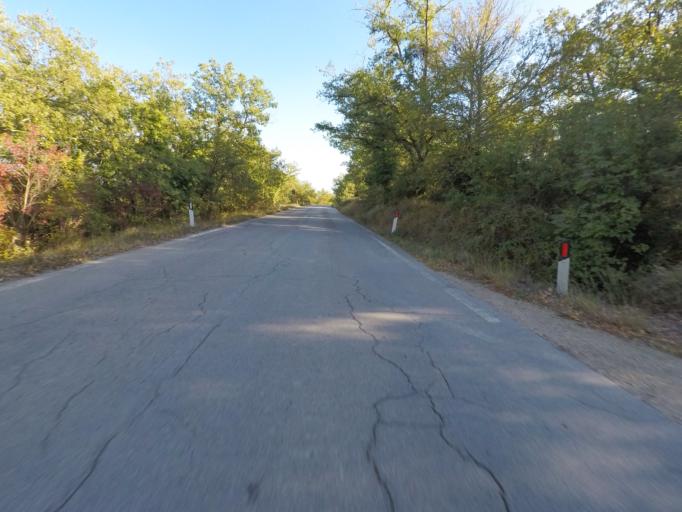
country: IT
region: Tuscany
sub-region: Provincia di Siena
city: Radda in Chianti
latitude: 43.4463
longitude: 11.3939
